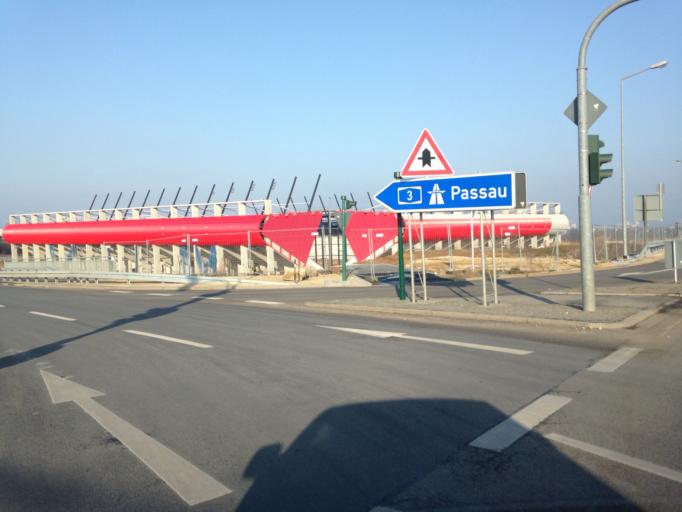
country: DE
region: Bavaria
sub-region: Upper Palatinate
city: Regensburg
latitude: 48.9893
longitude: 12.1057
